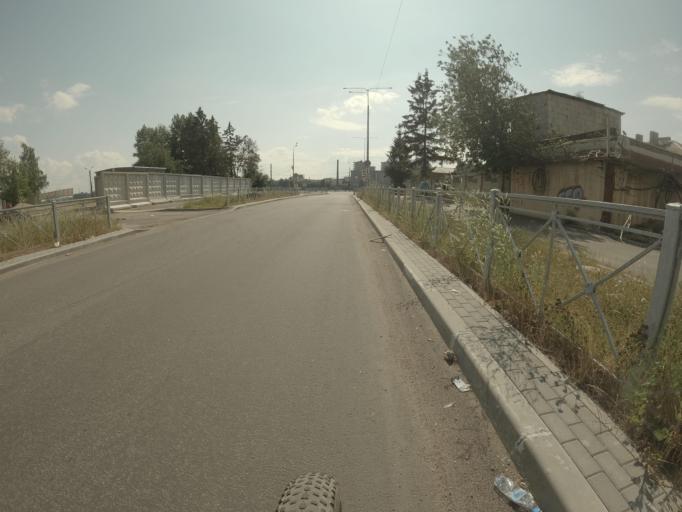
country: RU
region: St.-Petersburg
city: Obukhovo
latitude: 59.9041
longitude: 30.4387
